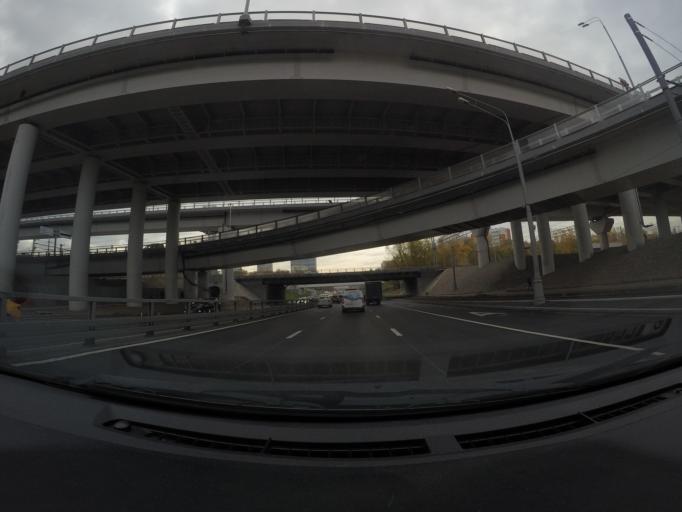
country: RU
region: Moscow
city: Rostokino
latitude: 55.8414
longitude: 37.6642
